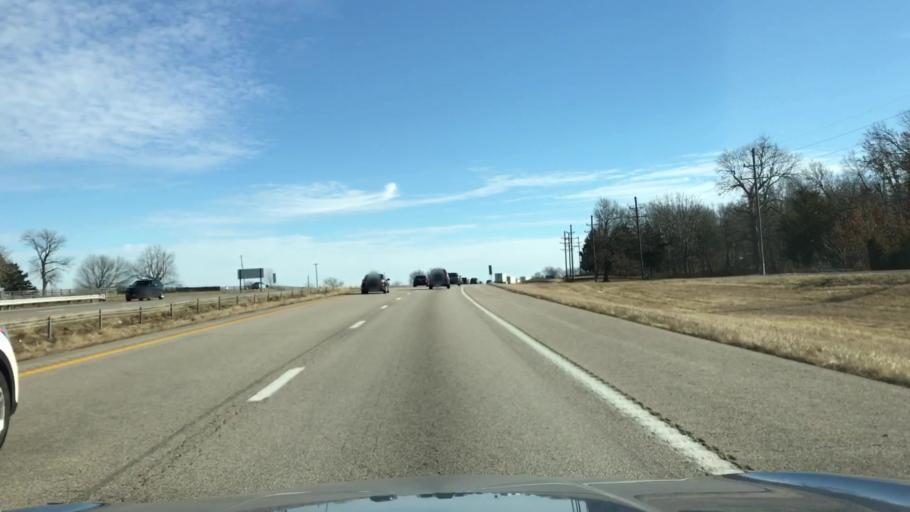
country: US
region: Missouri
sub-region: Warren County
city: Warrenton
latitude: 38.8458
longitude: -91.2373
